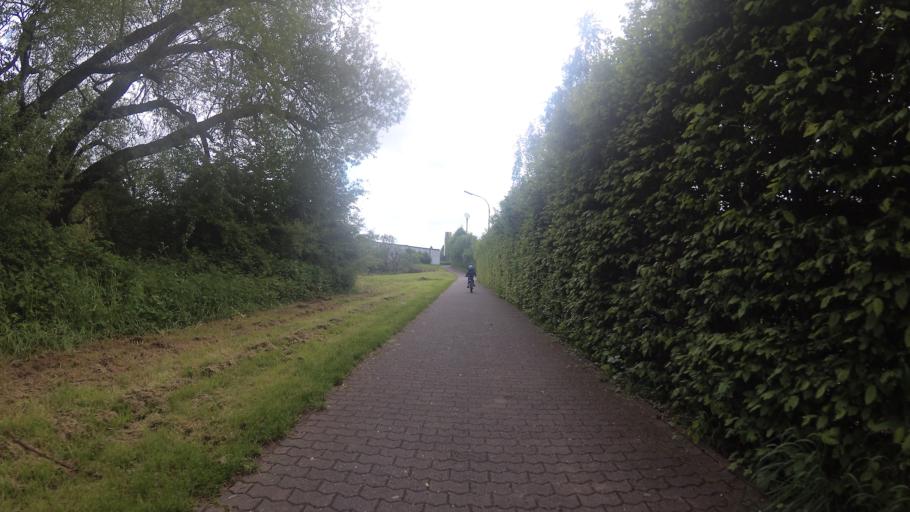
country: DE
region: Saarland
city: Lebach
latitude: 49.4104
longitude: 6.9021
